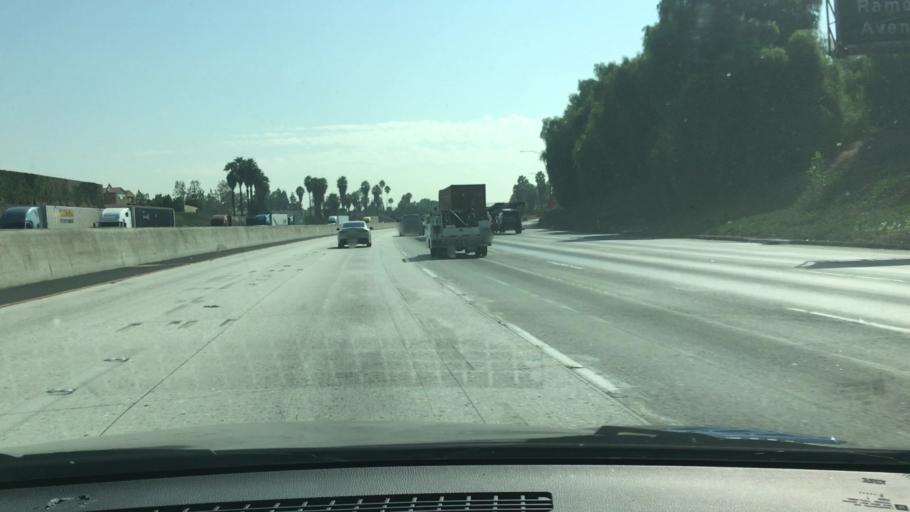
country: US
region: California
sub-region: San Bernardino County
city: Chino
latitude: 34.0298
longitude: -117.7124
